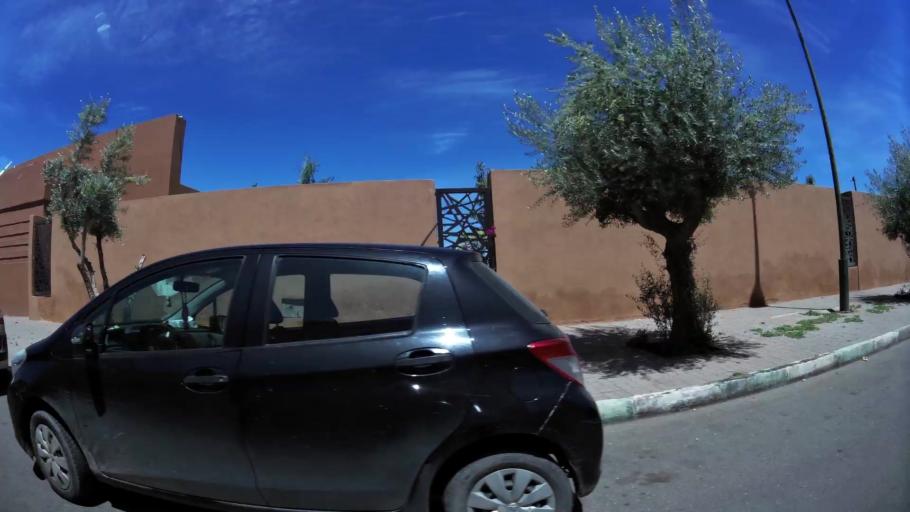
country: MA
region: Marrakech-Tensift-Al Haouz
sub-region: Marrakech
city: Marrakesh
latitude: 31.6310
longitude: -8.0441
